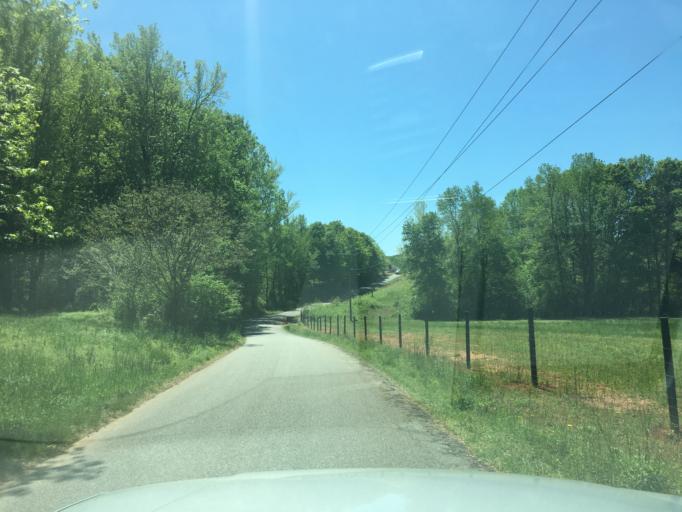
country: US
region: South Carolina
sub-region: Spartanburg County
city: Duncan
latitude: 34.8579
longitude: -82.1603
